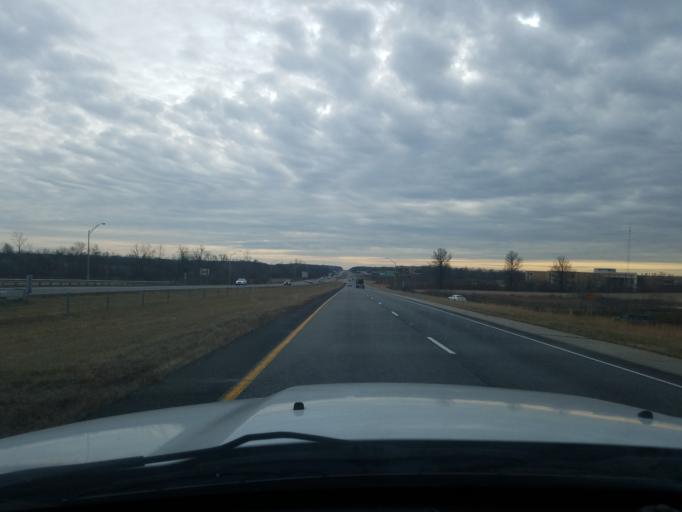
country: US
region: Indiana
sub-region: Grant County
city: Gas City
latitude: 40.5525
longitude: -85.5510
